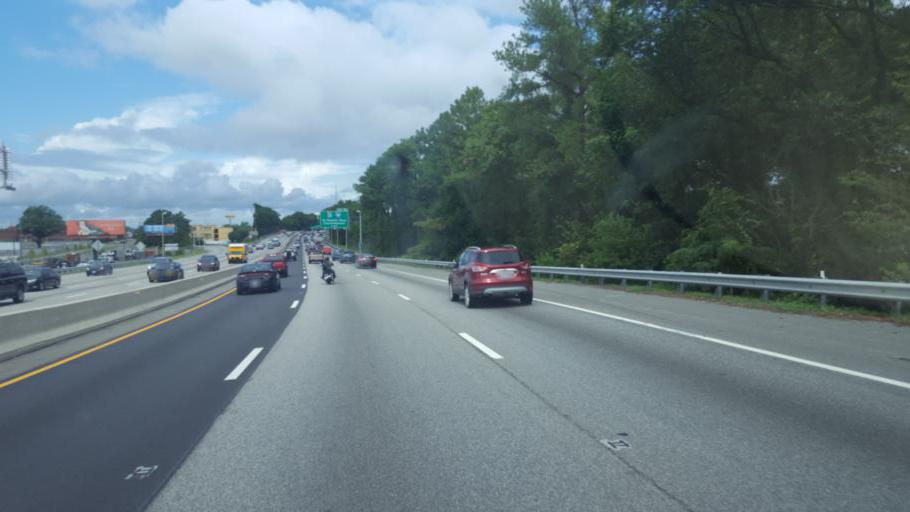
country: US
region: Virginia
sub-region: City of Richmond
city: Richmond
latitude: 37.5720
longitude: -77.4555
